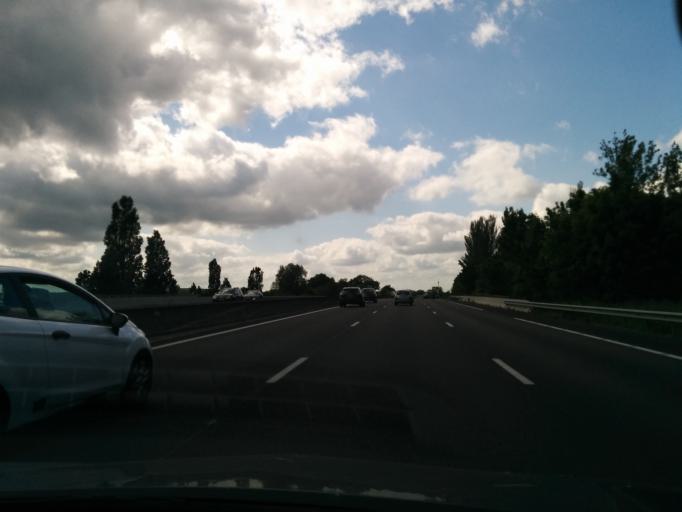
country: FR
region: Ile-de-France
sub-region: Departement des Yvelines
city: Orgeval
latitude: 48.9356
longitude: 1.9640
